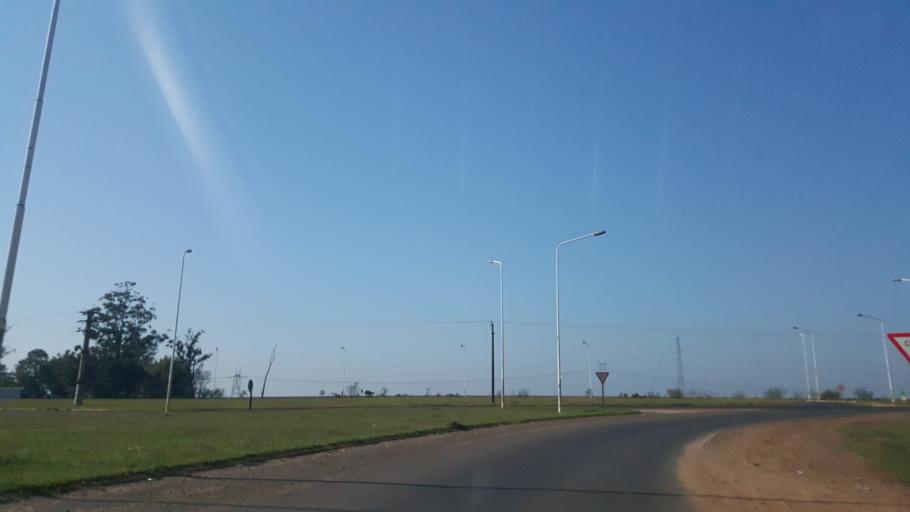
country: AR
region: Corrientes
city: Ituzaingo
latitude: -27.5993
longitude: -56.6743
